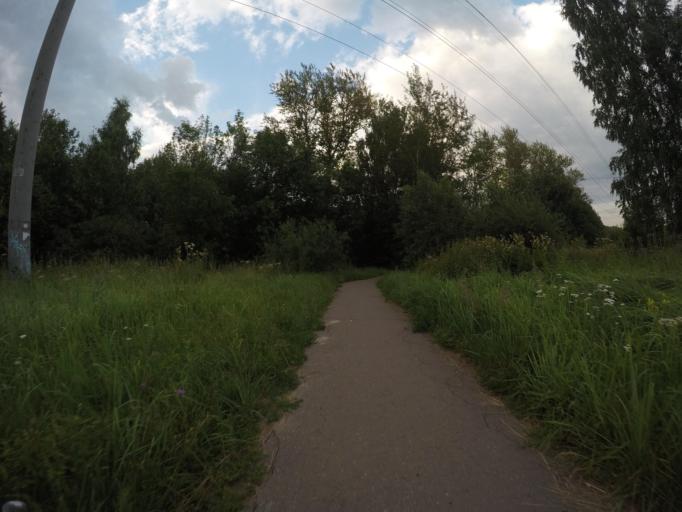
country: RU
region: Moskovskaya
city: Rechitsy
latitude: 55.6027
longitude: 38.5073
